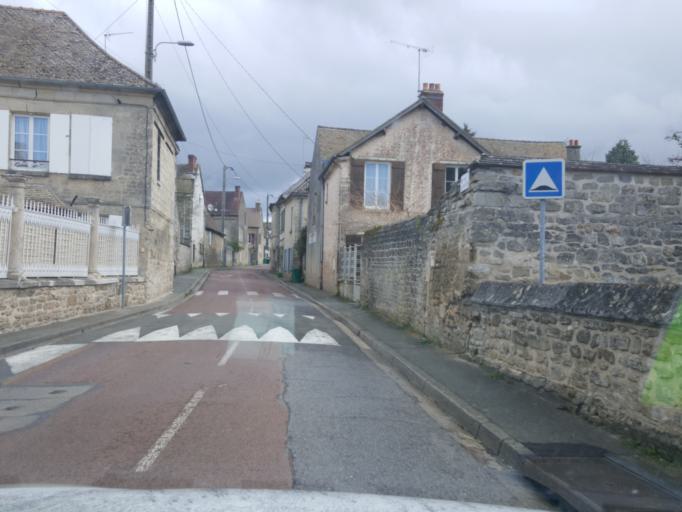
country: FR
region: Ile-de-France
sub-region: Departement du Val-d'Oise
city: Magny-en-Vexin
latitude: 49.1959
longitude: 1.8008
